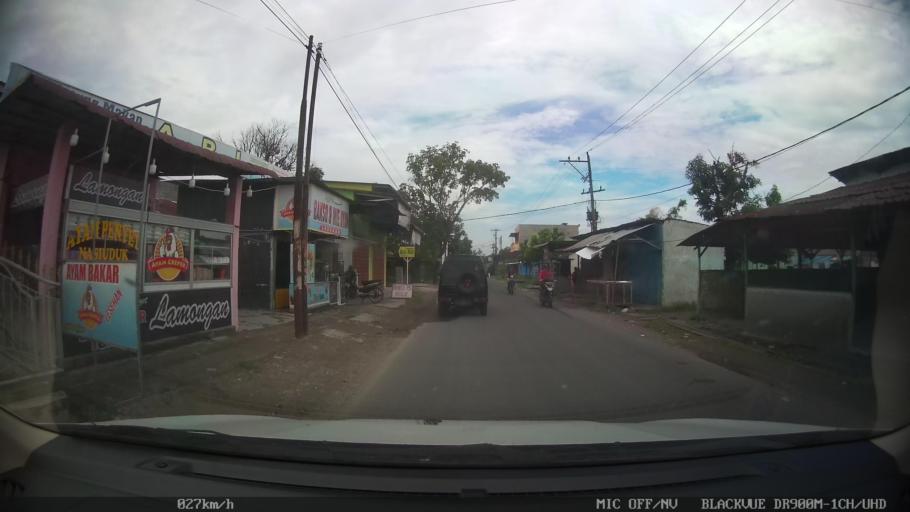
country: ID
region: North Sumatra
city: Sunggal
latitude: 3.6219
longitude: 98.5952
